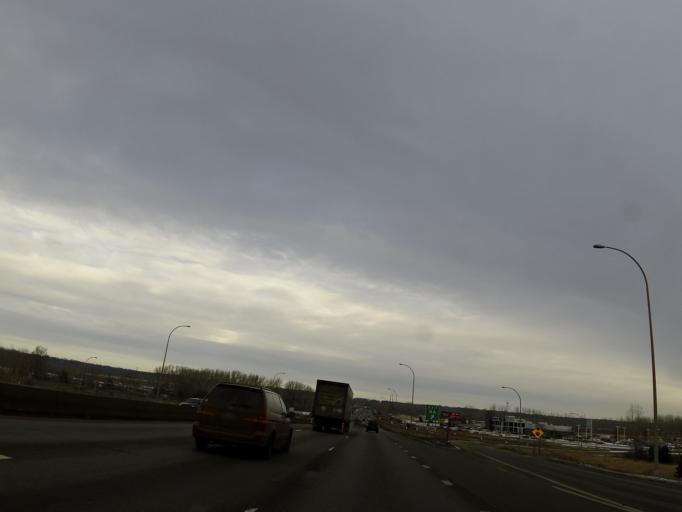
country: US
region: Minnesota
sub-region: Dakota County
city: Burnsville
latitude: 44.7826
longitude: -93.2884
